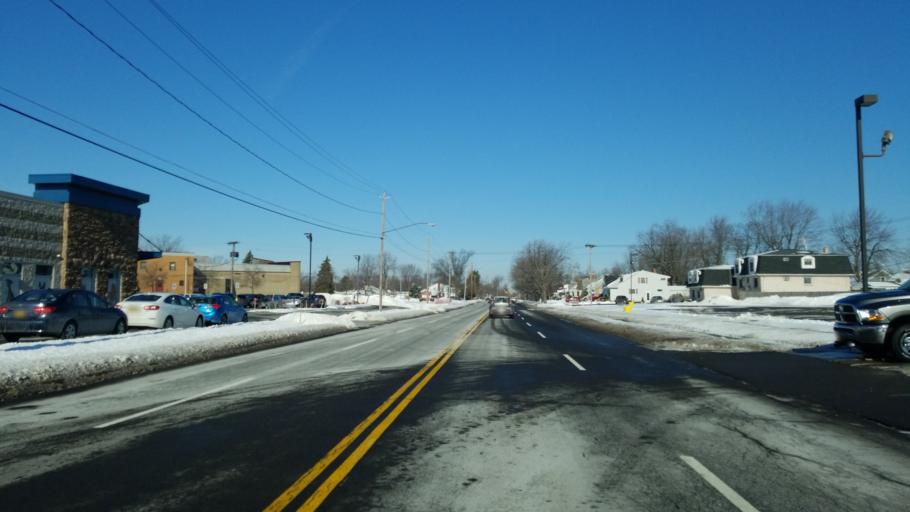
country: US
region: New York
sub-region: Erie County
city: Amherst
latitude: 42.9817
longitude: -78.8266
